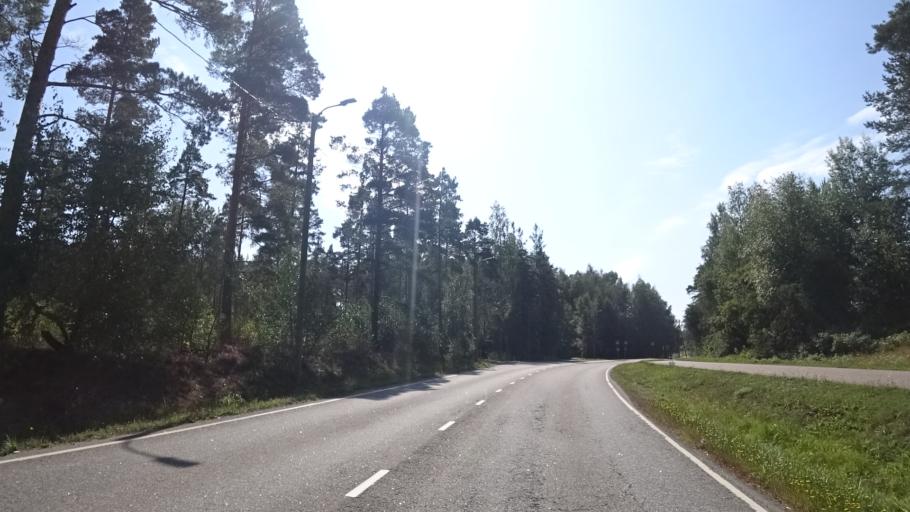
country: FI
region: Kymenlaakso
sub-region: Kotka-Hamina
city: Karhula
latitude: 60.5091
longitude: 26.9651
